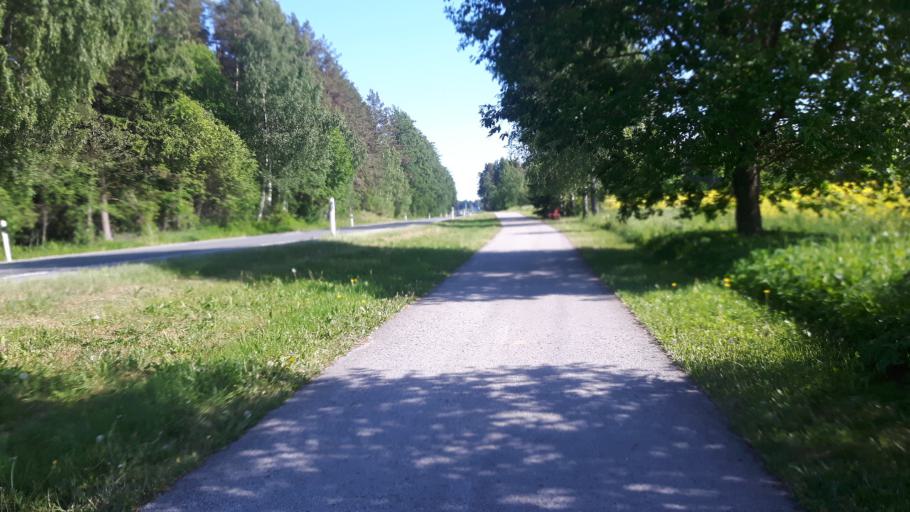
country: EE
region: Raplamaa
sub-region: Kehtna vald
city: Kehtna
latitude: 58.9725
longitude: 24.8503
